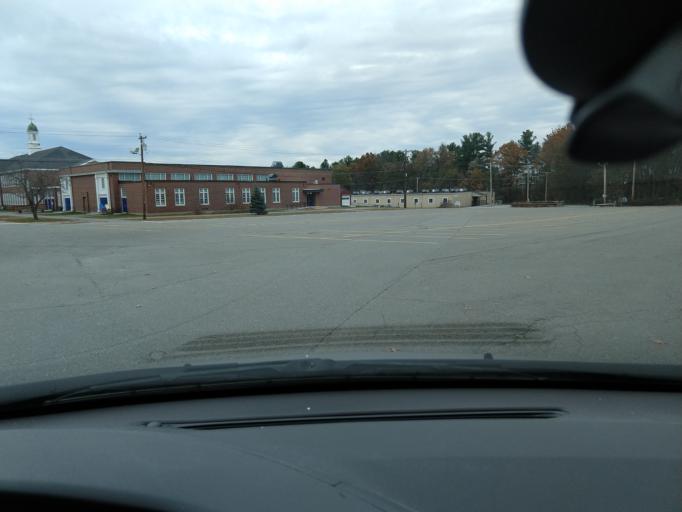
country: US
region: Massachusetts
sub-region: Middlesex County
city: Westford
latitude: 42.5876
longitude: -71.4330
